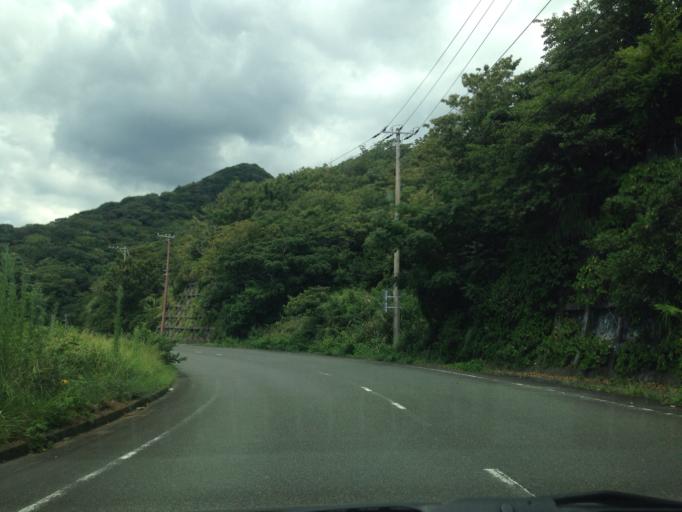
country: JP
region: Shizuoka
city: Shimoda
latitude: 34.6666
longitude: 138.7912
